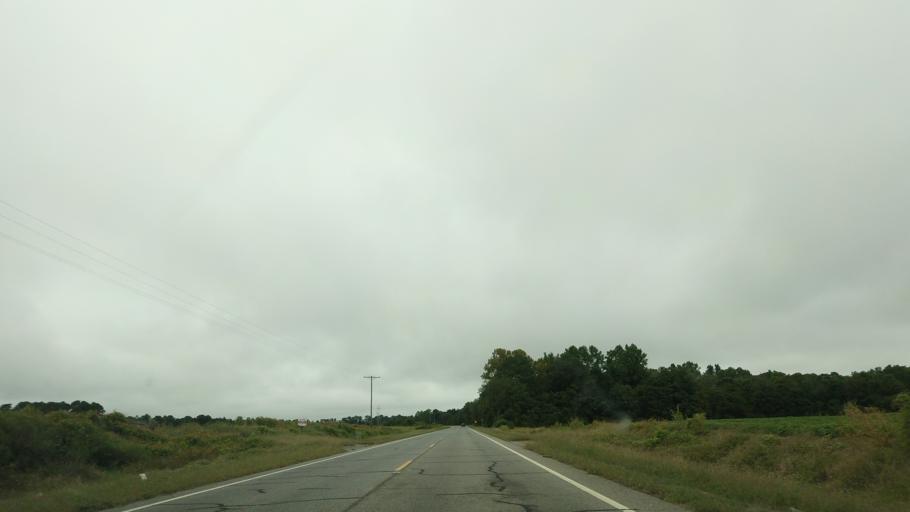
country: US
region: Georgia
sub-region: Irwin County
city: Ocilla
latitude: 31.5305
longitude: -83.2470
